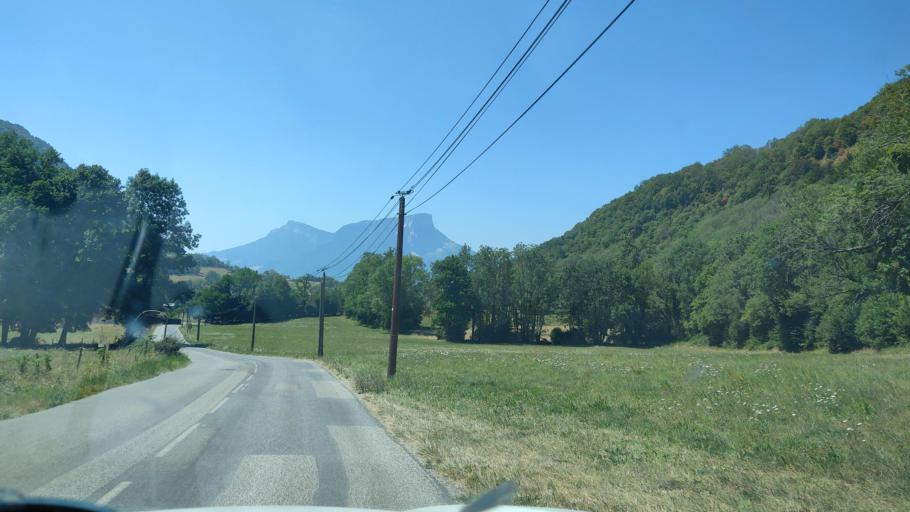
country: FR
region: Rhone-Alpes
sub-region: Departement de la Savoie
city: Challes-les-Eaux
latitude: 45.5583
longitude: 6.0187
